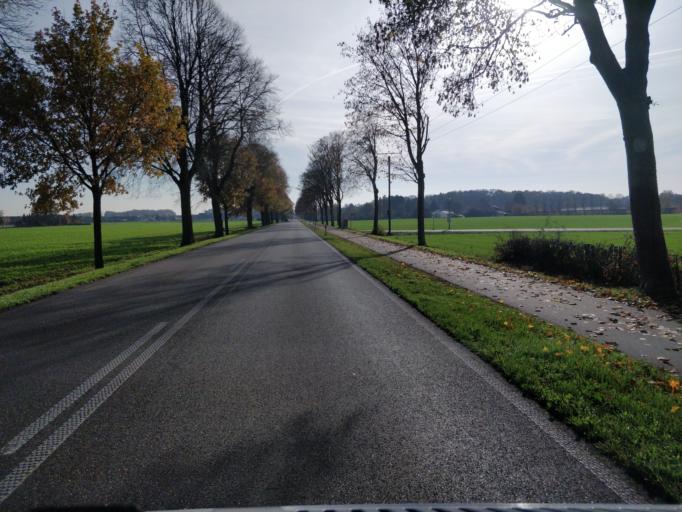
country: DE
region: North Rhine-Westphalia
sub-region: Regierungsbezirk Dusseldorf
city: Mehrhoog
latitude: 51.7438
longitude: 6.4935
